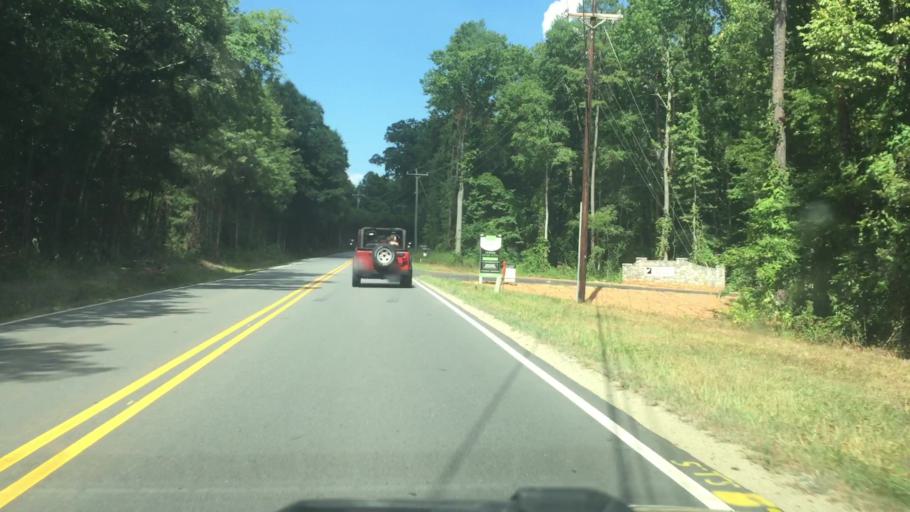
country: US
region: North Carolina
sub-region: Mecklenburg County
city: Huntersville
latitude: 35.4316
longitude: -80.7309
